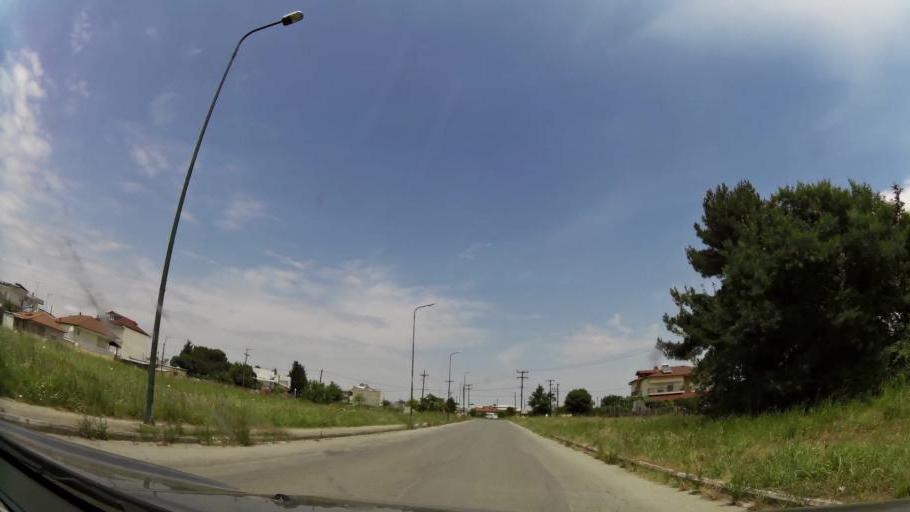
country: GR
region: Central Macedonia
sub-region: Nomos Pierias
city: Peristasi
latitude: 40.2672
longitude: 22.5349
